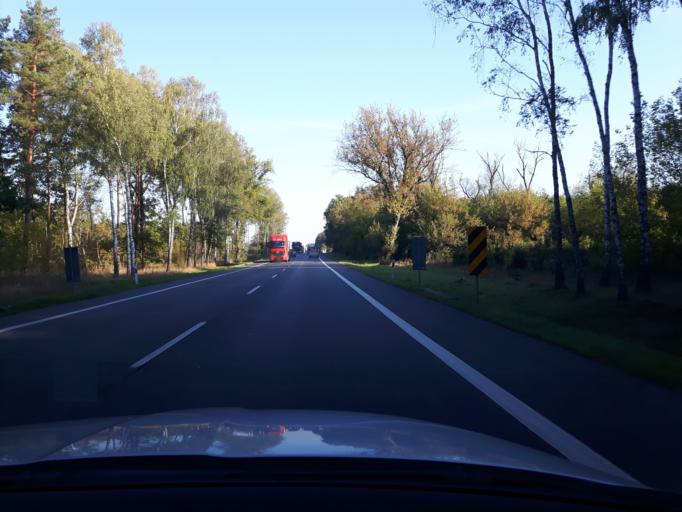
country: PL
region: Masovian Voivodeship
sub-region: Powiat mlawski
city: Strzegowo
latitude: 52.9172
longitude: 20.2865
